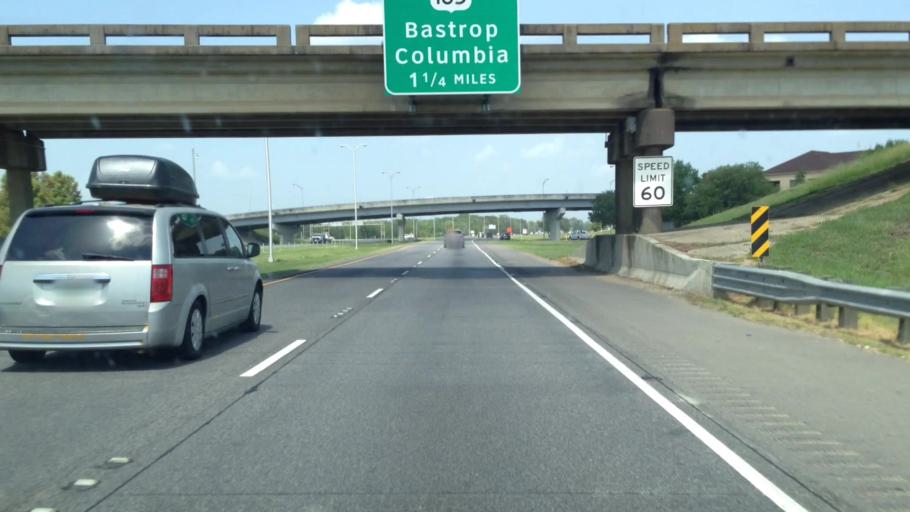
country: US
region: Louisiana
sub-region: Ouachita Parish
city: Lakeshore
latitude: 32.4946
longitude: -92.0541
